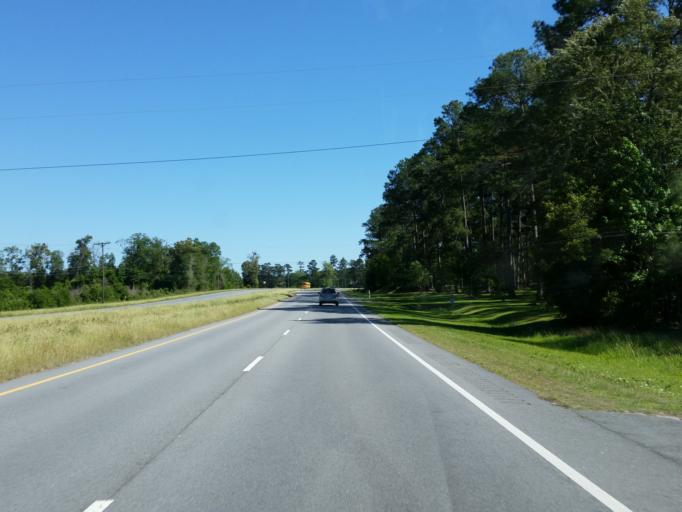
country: US
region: Georgia
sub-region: Lowndes County
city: Valdosta
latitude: 30.7248
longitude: -83.2180
